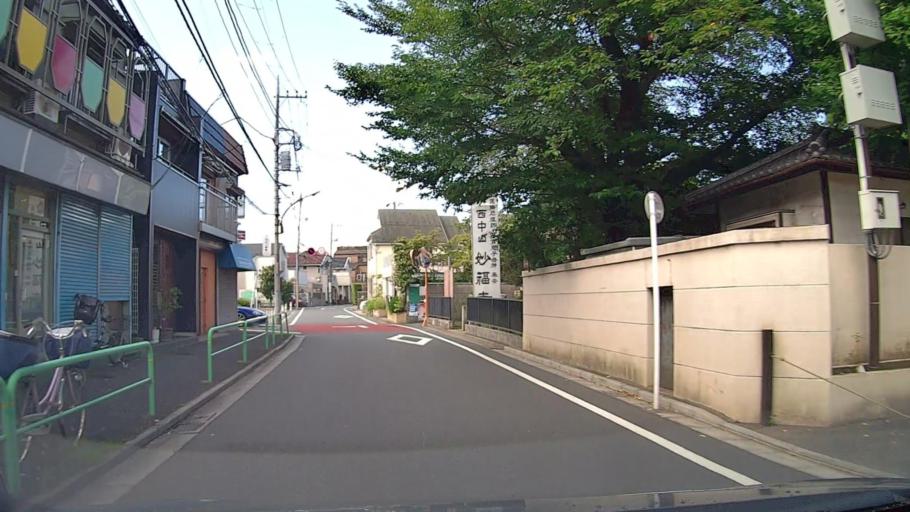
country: JP
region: Tokyo
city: Nishi-Tokyo-shi
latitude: 35.7508
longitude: 139.5793
